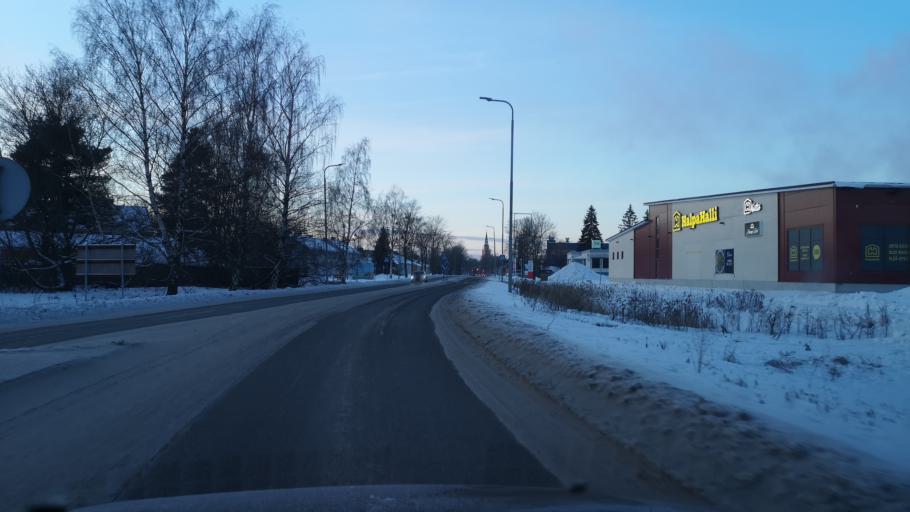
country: FI
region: Satakunta
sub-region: Pori
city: Pori
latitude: 61.4816
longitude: 21.8149
